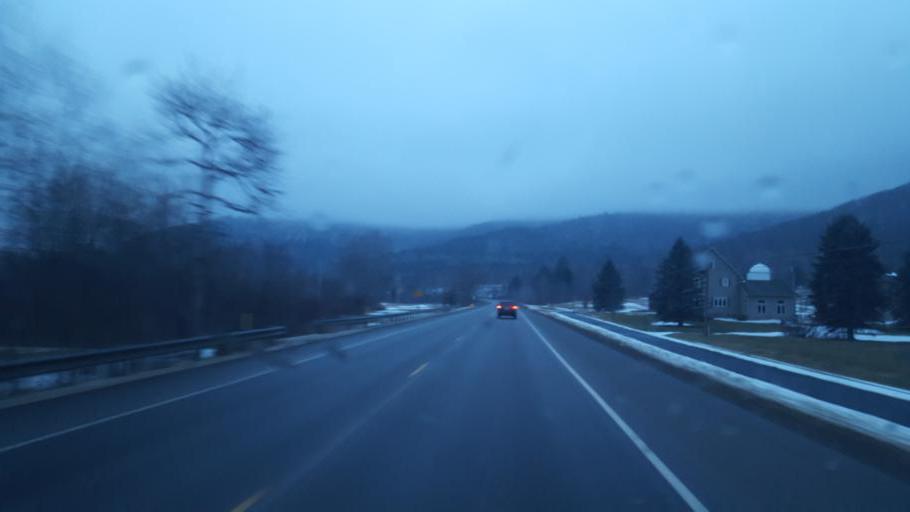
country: US
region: Pennsylvania
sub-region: McKean County
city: Port Allegany
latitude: 41.7902
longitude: -78.2088
